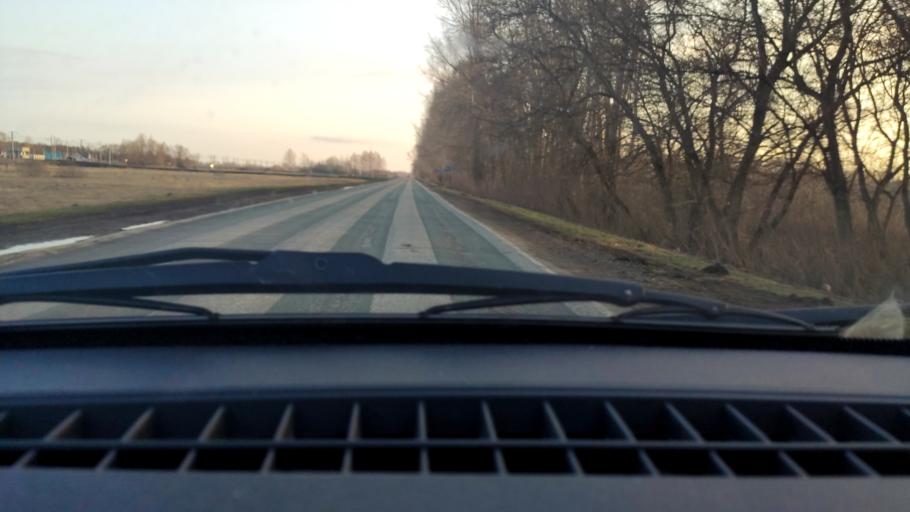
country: RU
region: Bashkortostan
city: Chishmy
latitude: 54.4534
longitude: 55.2500
